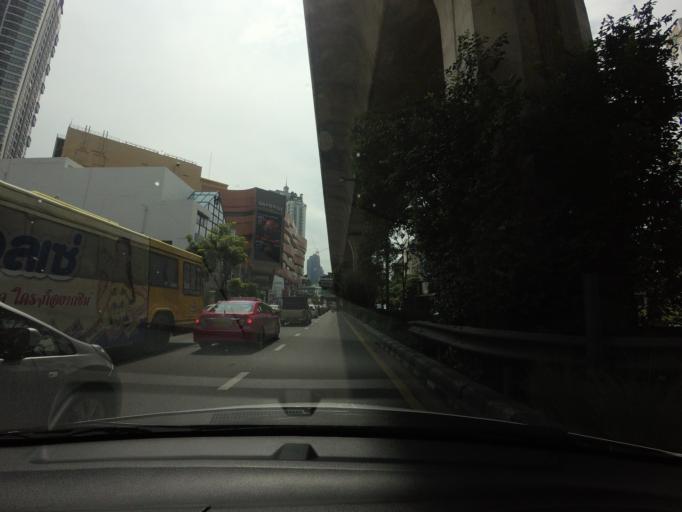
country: TH
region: Bangkok
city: Watthana
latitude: 13.7184
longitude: 100.5867
